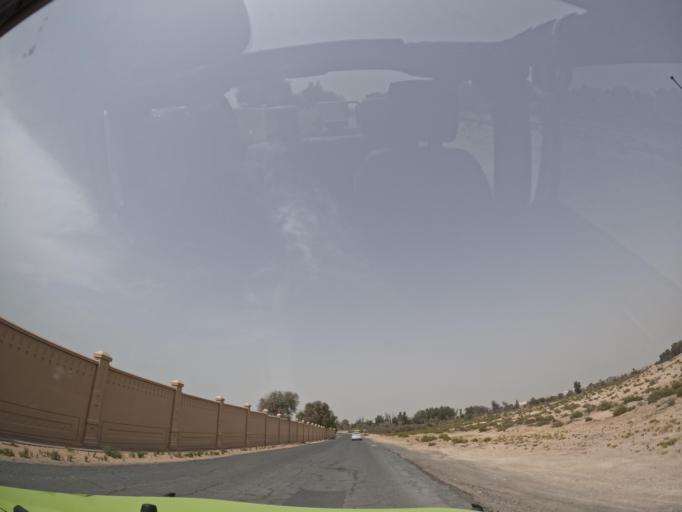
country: AE
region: Dubai
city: Dubai
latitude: 25.1375
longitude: 55.3386
